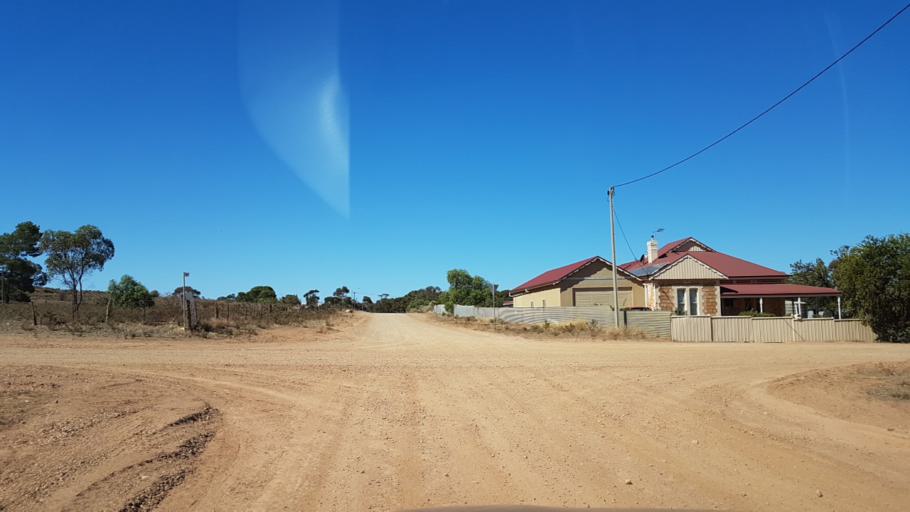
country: AU
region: South Australia
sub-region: Peterborough
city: Peterborough
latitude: -32.9695
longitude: 138.8254
